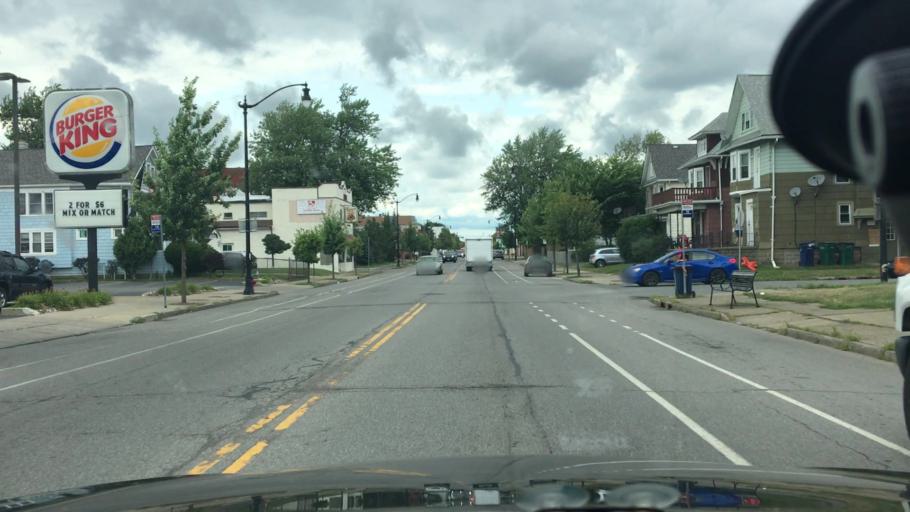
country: US
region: New York
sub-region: Erie County
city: Lackawanna
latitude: 42.8345
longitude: -78.8239
